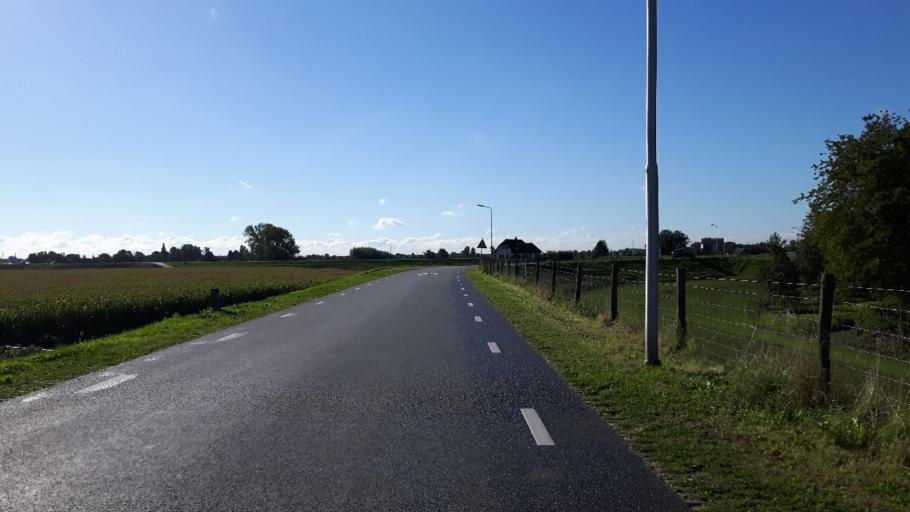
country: NL
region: Utrecht
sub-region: Gemeente Vianen
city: Vianen
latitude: 51.9862
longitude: 5.1349
